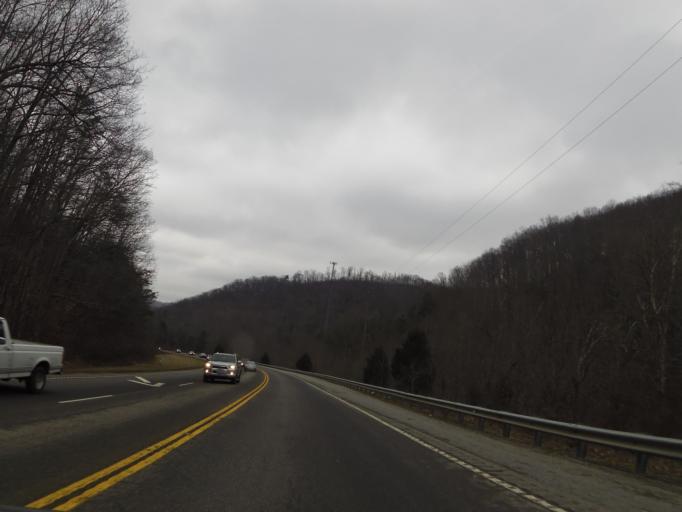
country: US
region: Tennessee
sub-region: Campbell County
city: Caryville
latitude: 36.3967
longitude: -84.3125
